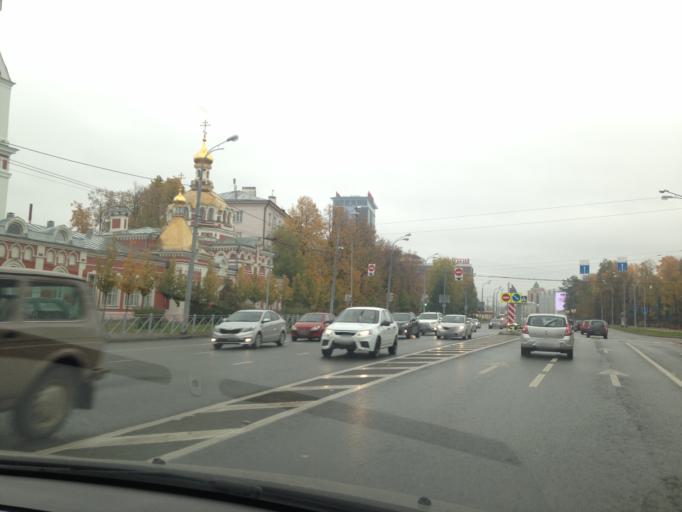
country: RU
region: Tatarstan
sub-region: Gorod Kazan'
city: Kazan
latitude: 55.7945
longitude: 49.1423
